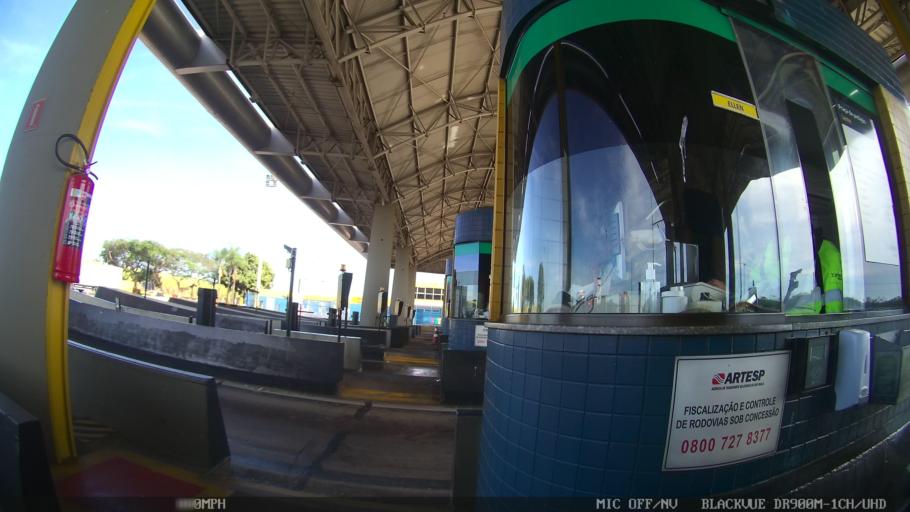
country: BR
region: Sao Paulo
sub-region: Leme
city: Leme
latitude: -22.2499
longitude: -47.3900
